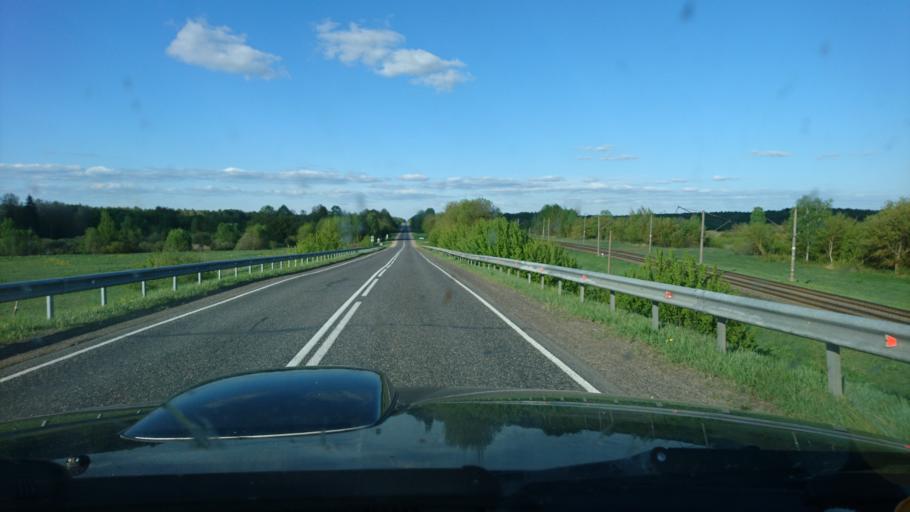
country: BY
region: Brest
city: Nyakhachava
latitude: 52.6397
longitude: 25.1968
